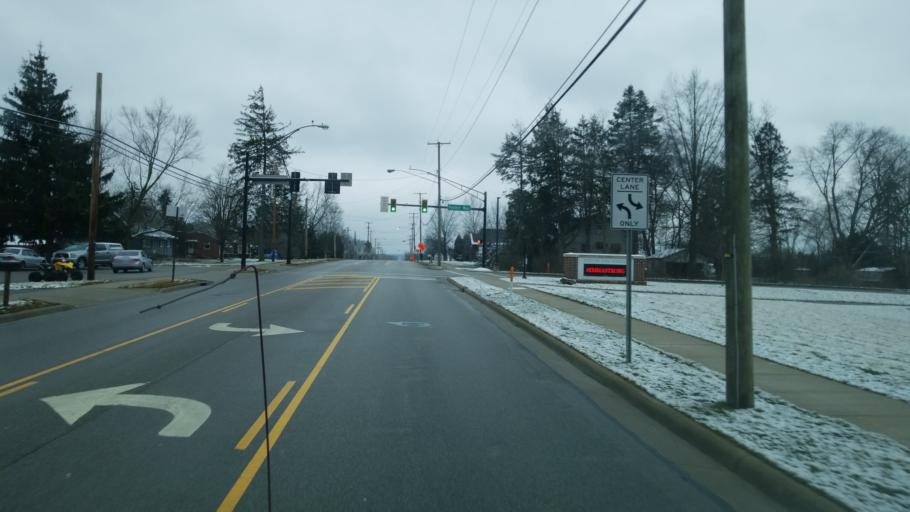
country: US
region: Ohio
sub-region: Summit County
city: Norton
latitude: 41.0336
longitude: -81.6381
